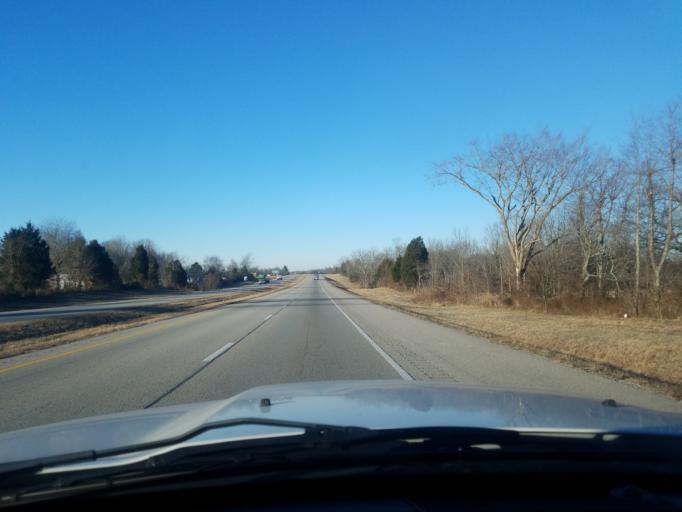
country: US
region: Kentucky
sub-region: Grayson County
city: Leitchfield
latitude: 37.4942
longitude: -86.1893
